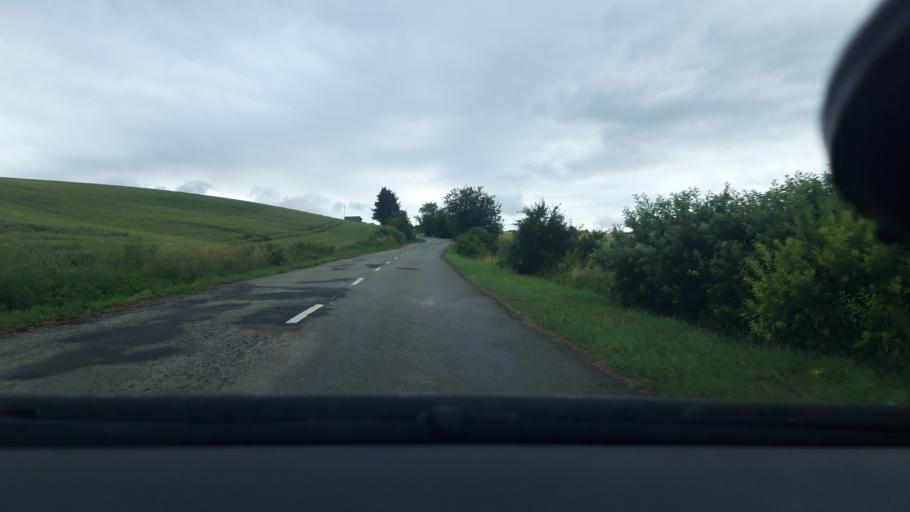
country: SK
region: Zilinsky
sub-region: Okres Martin
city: Martin
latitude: 49.0178
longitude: 18.9947
